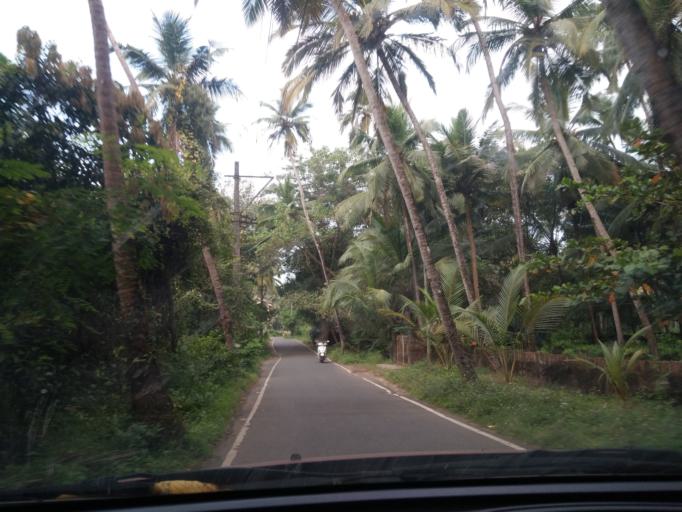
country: IN
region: Goa
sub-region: South Goa
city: Varca
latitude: 15.2314
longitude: 73.9479
